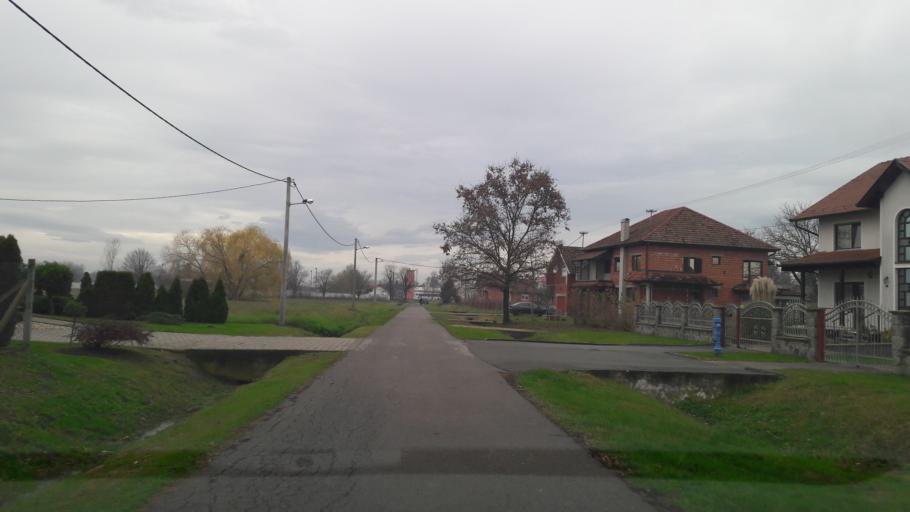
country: HR
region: Osjecko-Baranjska
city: Koska
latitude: 45.5426
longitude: 18.2888
